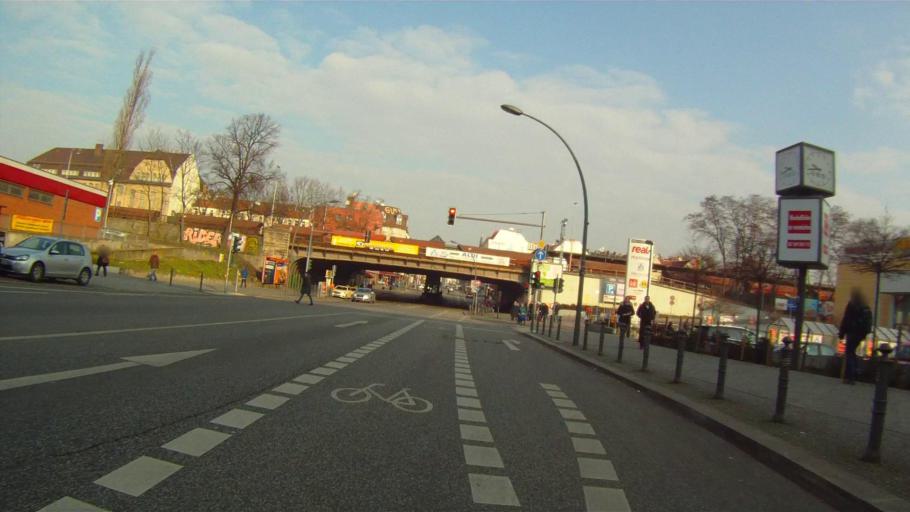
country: DE
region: Berlin
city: Berlin Treptow
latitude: 52.4683
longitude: 13.4420
